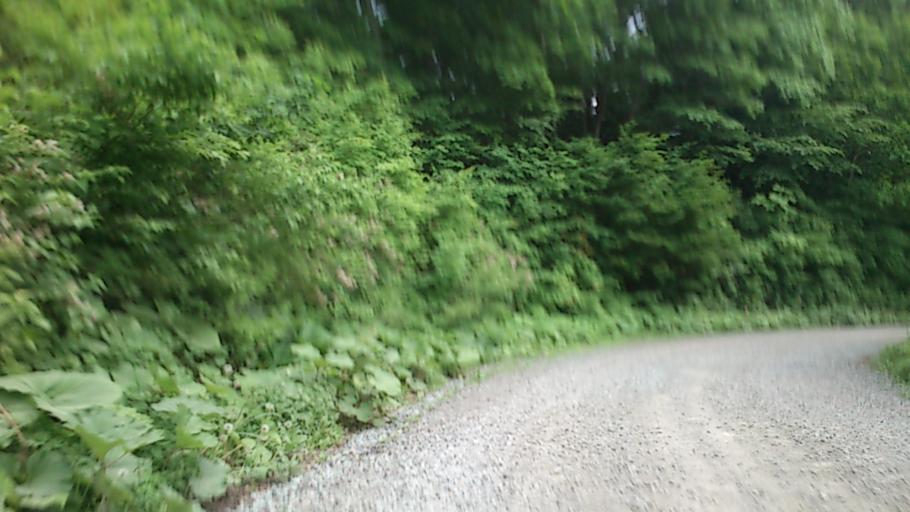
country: JP
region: Aomori
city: Hirosaki
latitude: 40.5592
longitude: 140.1835
